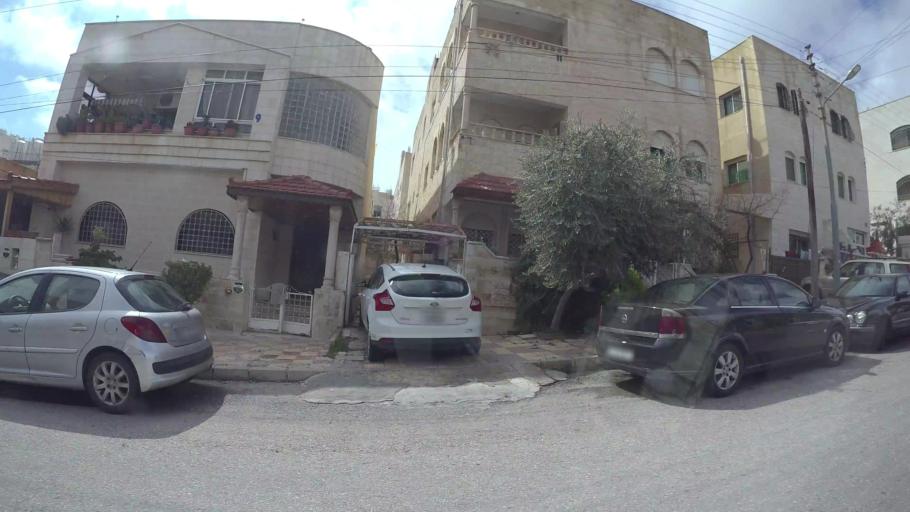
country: JO
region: Amman
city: Al Jubayhah
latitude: 32.0633
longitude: 35.8800
